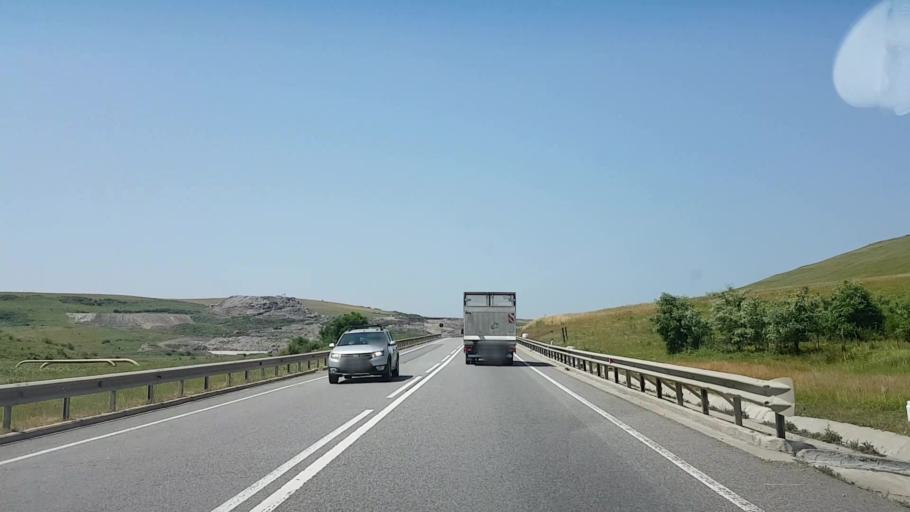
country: RO
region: Cluj
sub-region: Comuna Apahida
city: Dezmir
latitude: 46.7585
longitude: 23.6963
